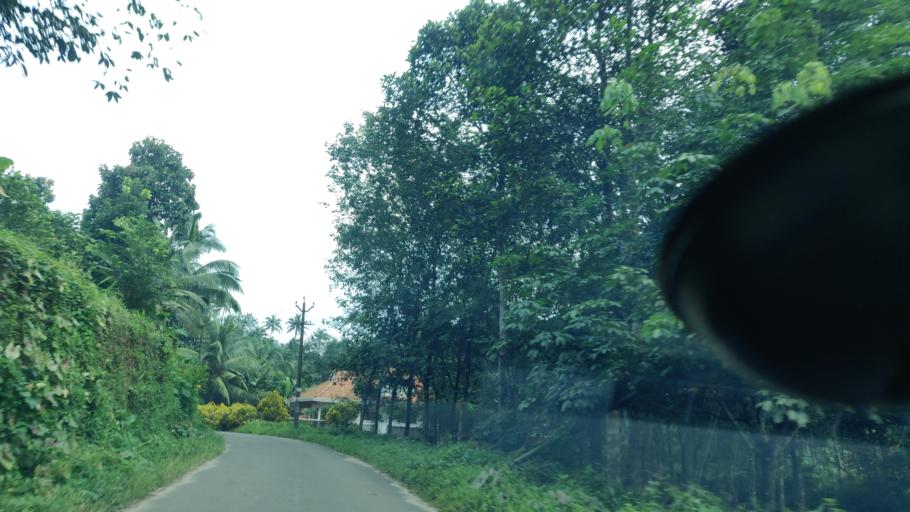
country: IN
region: Kerala
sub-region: Kottayam
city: Lalam
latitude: 9.8419
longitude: 76.7076
